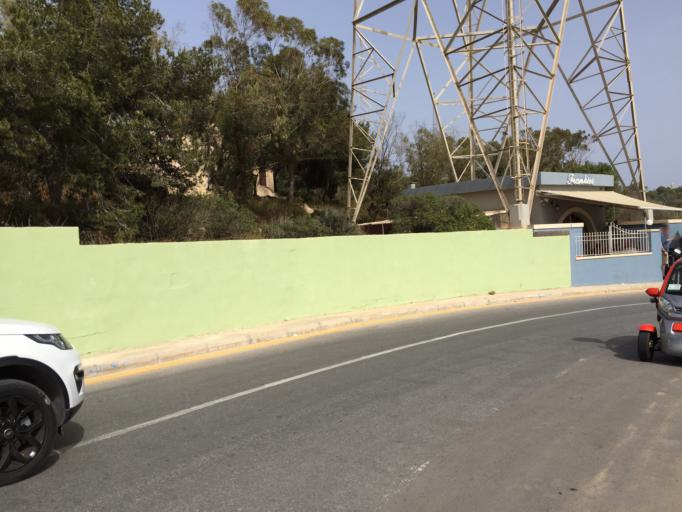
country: MT
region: Il-Kalkara
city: Kalkara
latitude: 35.8938
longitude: 14.5278
